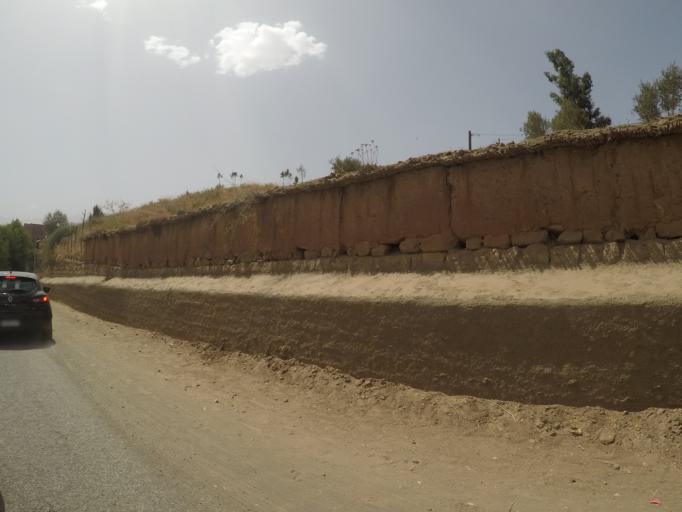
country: MA
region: Marrakech-Tensift-Al Haouz
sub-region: Al-Haouz
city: Moulay Brahim
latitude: 31.2351
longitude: -7.9754
